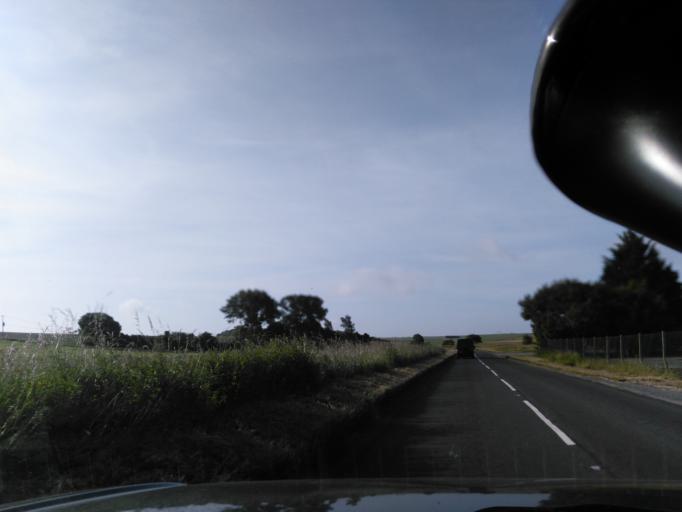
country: GB
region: England
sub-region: Wiltshire
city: Shrewton
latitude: 51.2200
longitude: -1.9439
